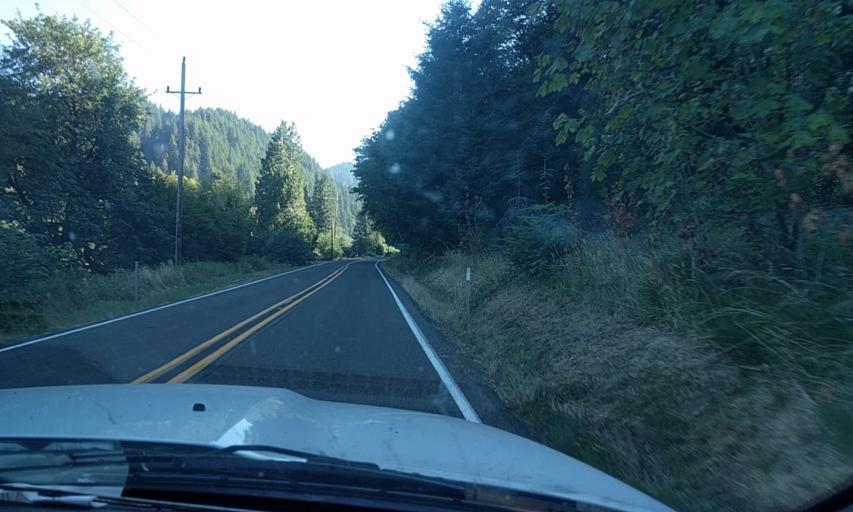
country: US
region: Oregon
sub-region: Lane County
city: Florence
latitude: 44.0722
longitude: -123.8774
